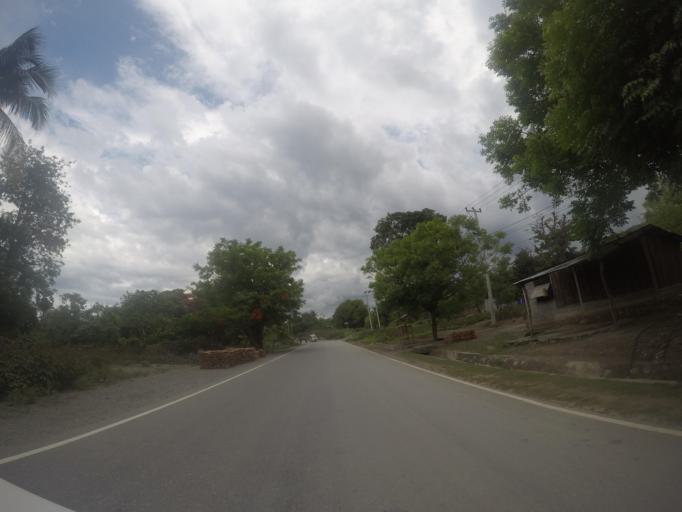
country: TL
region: Liquica
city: Liquica
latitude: -8.6033
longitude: 125.2992
